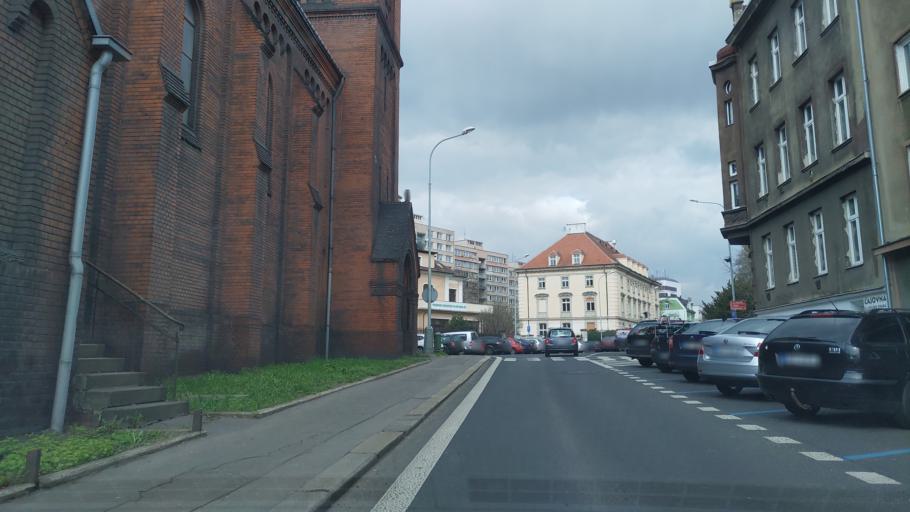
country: CZ
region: Ustecky
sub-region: Okres Usti nad Labem
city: Usti nad Labem
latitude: 50.6624
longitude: 14.0370
